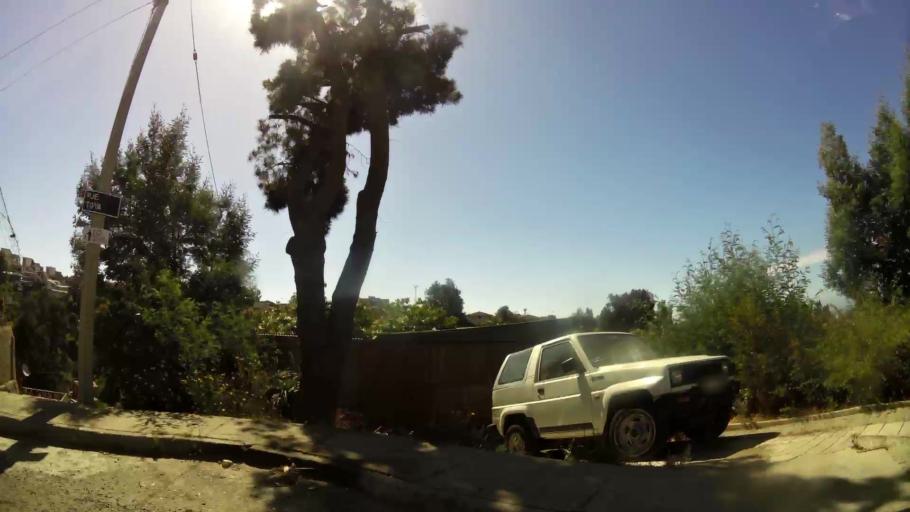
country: CL
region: Valparaiso
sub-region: Provincia de Valparaiso
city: Vina del Mar
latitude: -33.0341
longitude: -71.5760
